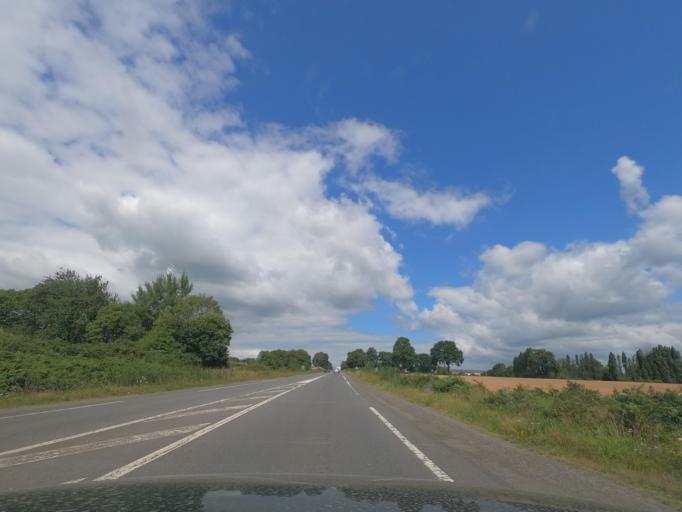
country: FR
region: Brittany
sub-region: Departement d'Ille-et-Vilaine
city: Lecousse
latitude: 48.3560
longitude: -1.2301
